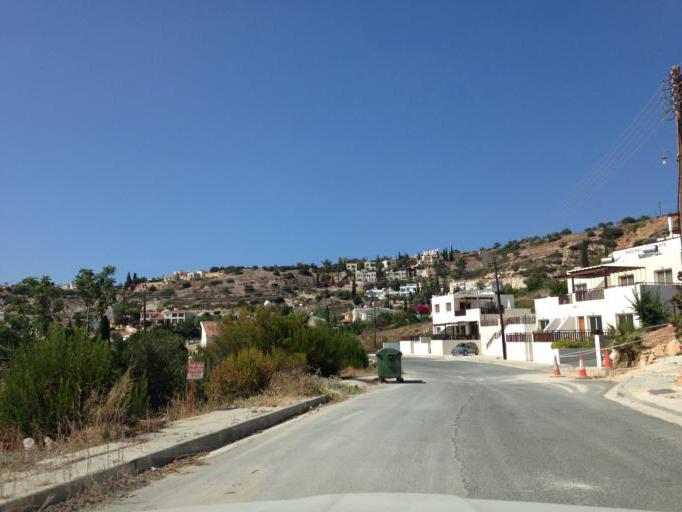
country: CY
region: Pafos
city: Pegeia
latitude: 34.8825
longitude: 32.3730
